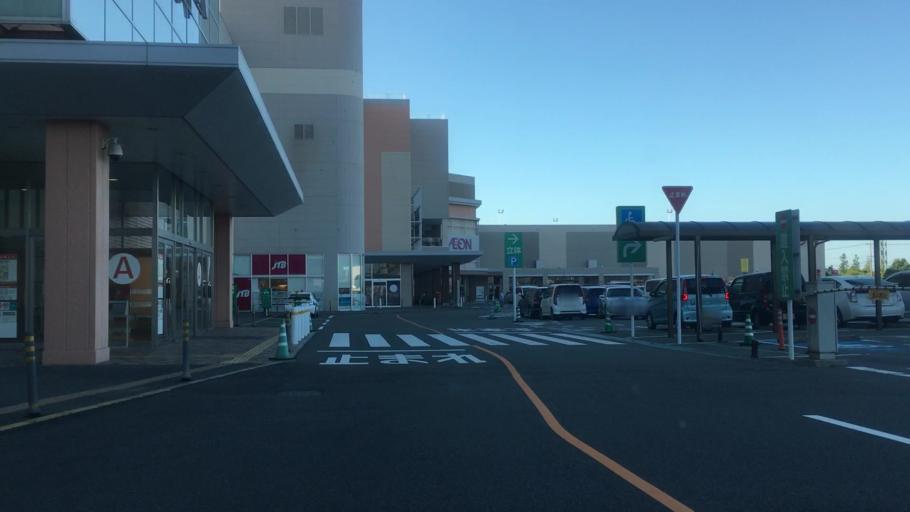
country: JP
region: Tottori
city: Tottori
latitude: 35.5230
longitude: 134.2015
